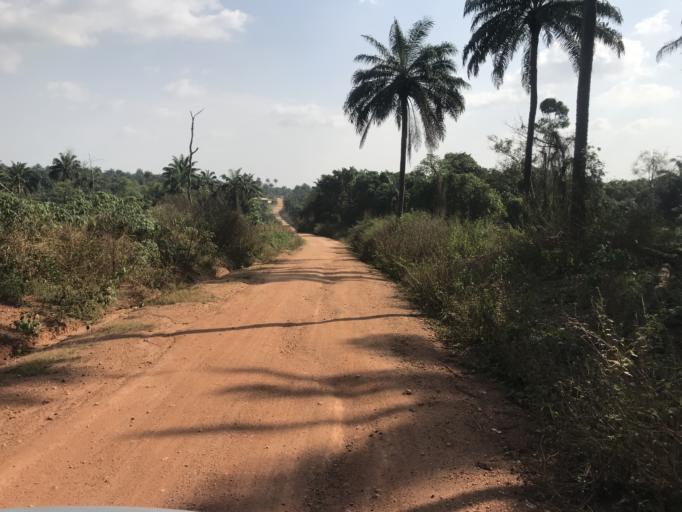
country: NG
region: Osun
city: Ikirun
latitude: 7.8666
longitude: 4.5870
